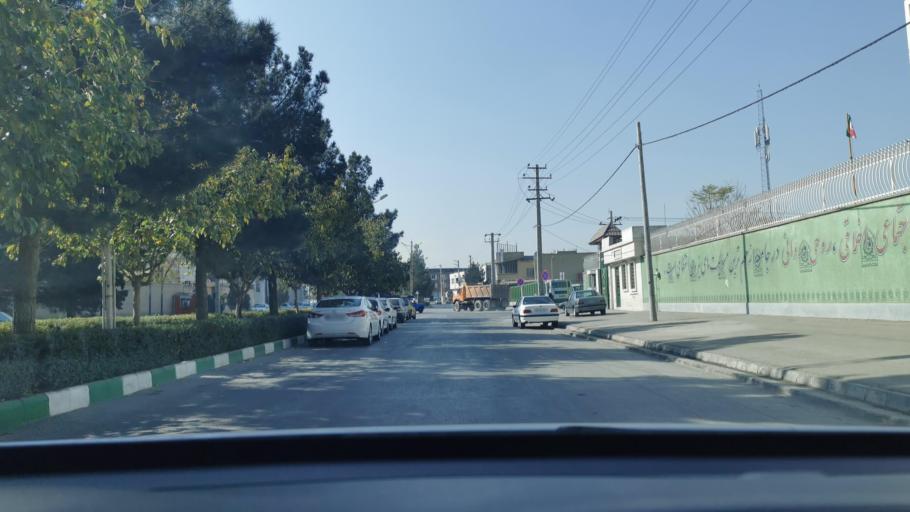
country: IR
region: Razavi Khorasan
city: Mashhad
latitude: 36.3488
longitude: 59.5989
